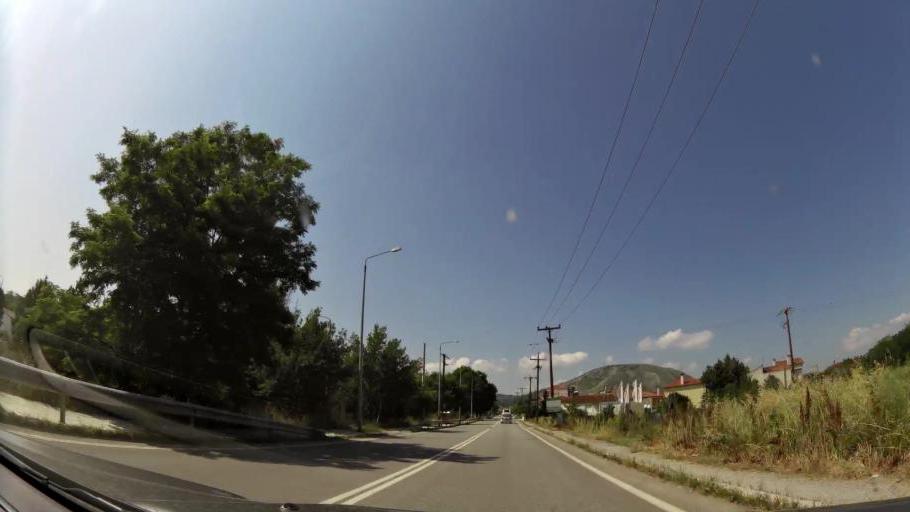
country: GR
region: West Macedonia
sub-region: Nomos Kozanis
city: Koila
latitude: 40.3338
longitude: 21.7909
